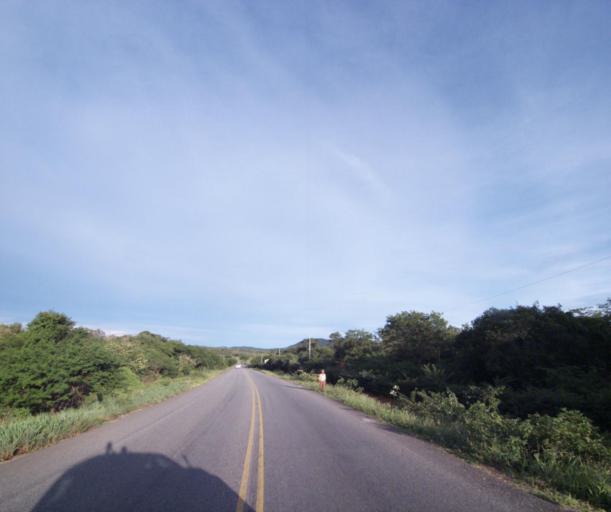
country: BR
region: Bahia
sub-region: Caetite
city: Caetite
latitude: -14.1787
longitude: -42.1724
